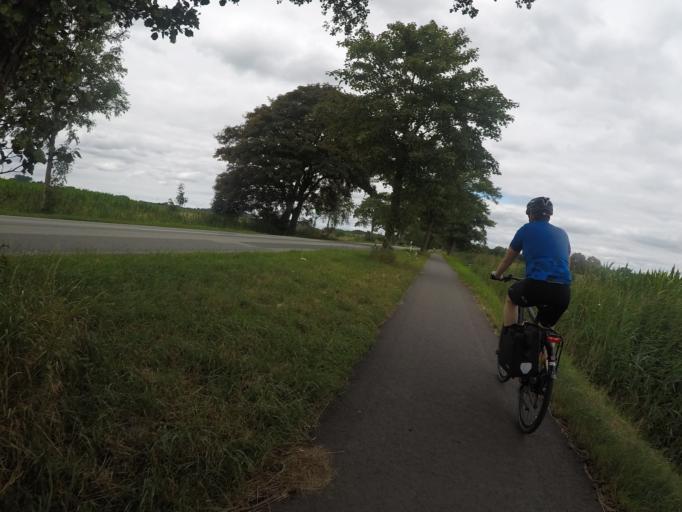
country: DE
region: Lower Saxony
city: Himmelpforten
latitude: 53.6424
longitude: 9.2972
